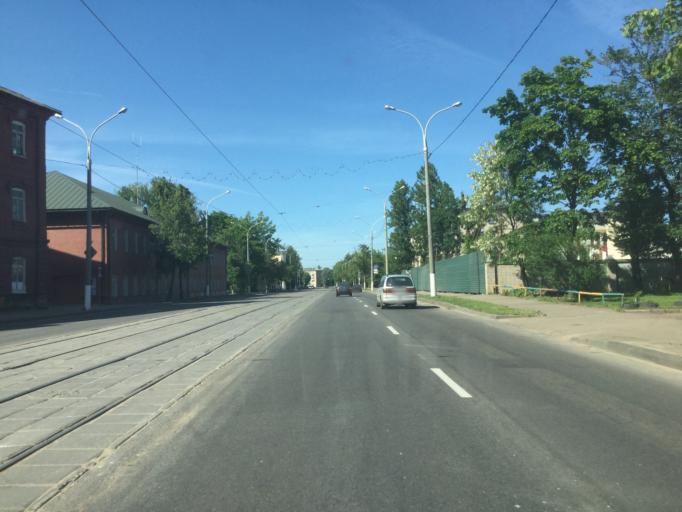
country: BY
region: Vitebsk
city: Vitebsk
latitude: 55.1864
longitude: 30.1889
